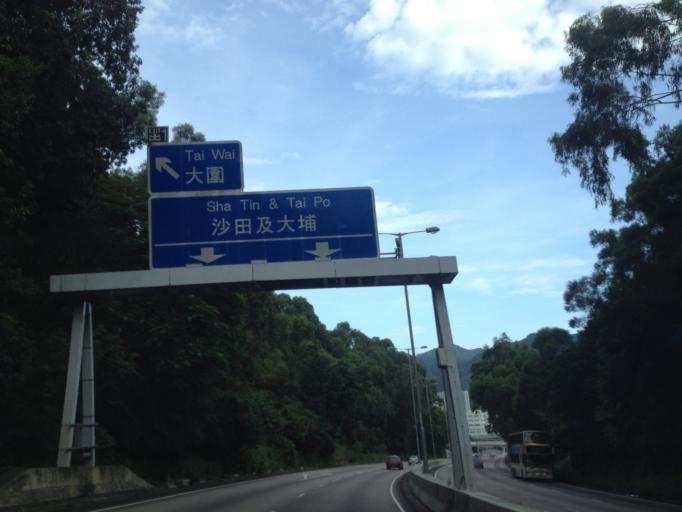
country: HK
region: Sha Tin
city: Sha Tin
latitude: 22.3823
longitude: 114.1746
